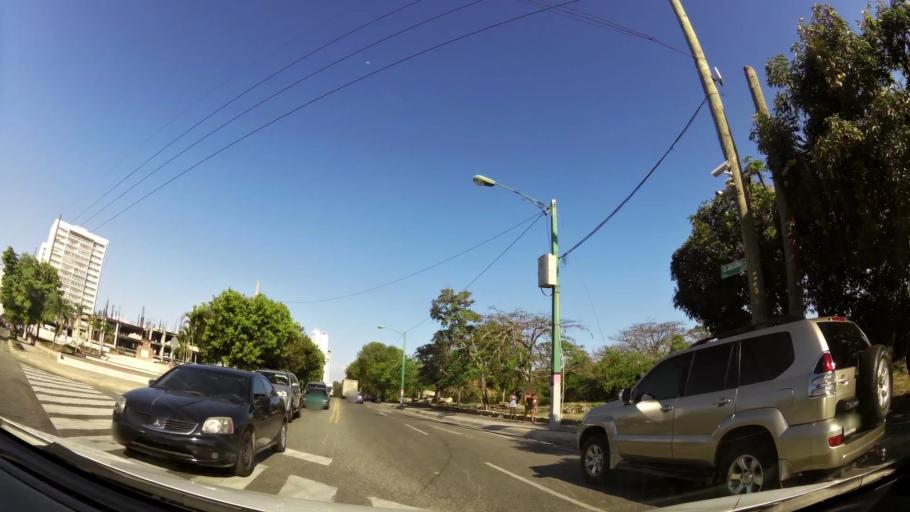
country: DO
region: Nacional
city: Bella Vista
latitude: 18.4364
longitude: -69.9822
